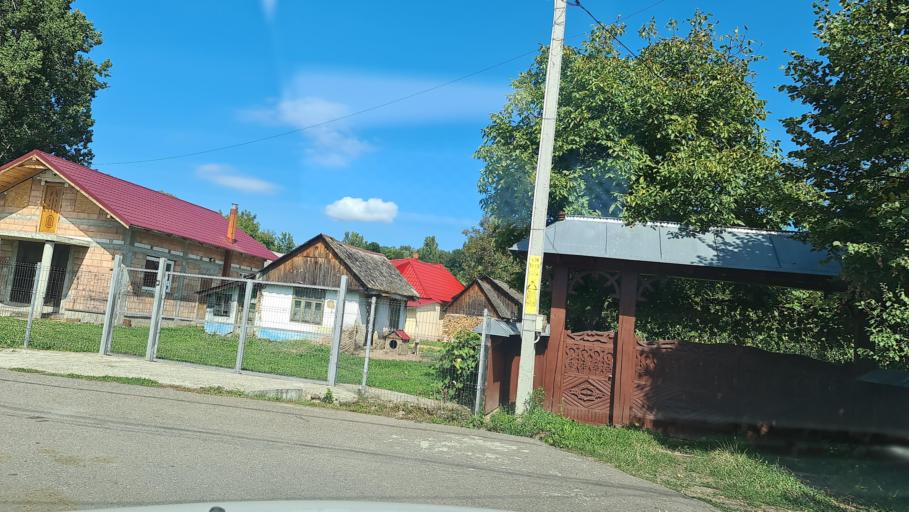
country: RO
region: Neamt
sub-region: Comuna Tazlau
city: Tazlau
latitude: 46.7139
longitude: 26.4838
